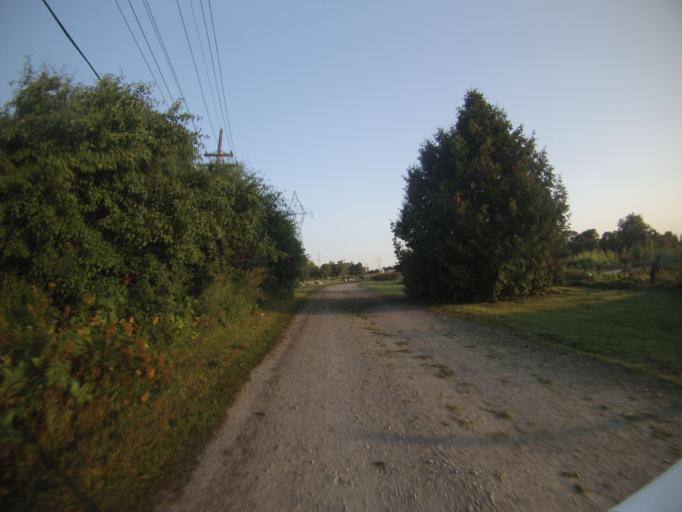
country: CA
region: Ontario
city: Ottawa
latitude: 45.3907
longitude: -75.6397
